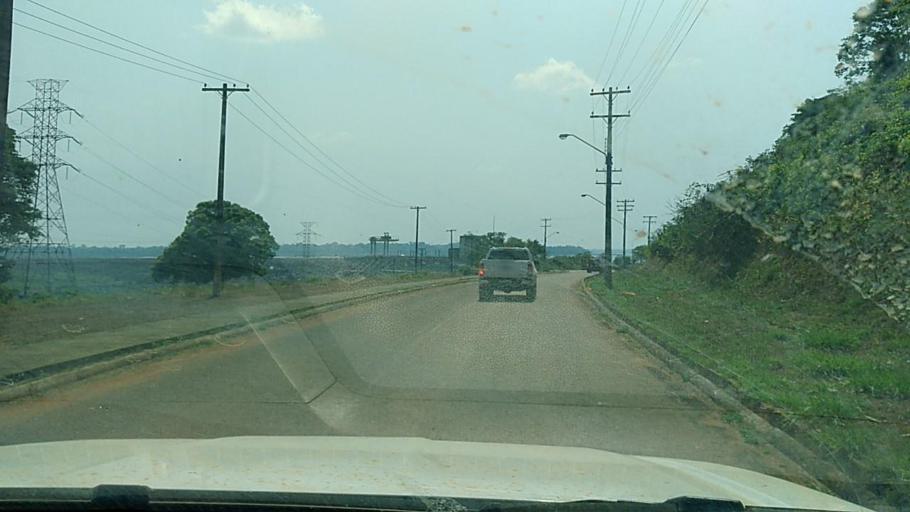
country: BR
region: Rondonia
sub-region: Porto Velho
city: Porto Velho
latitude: -8.7540
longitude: -63.4597
